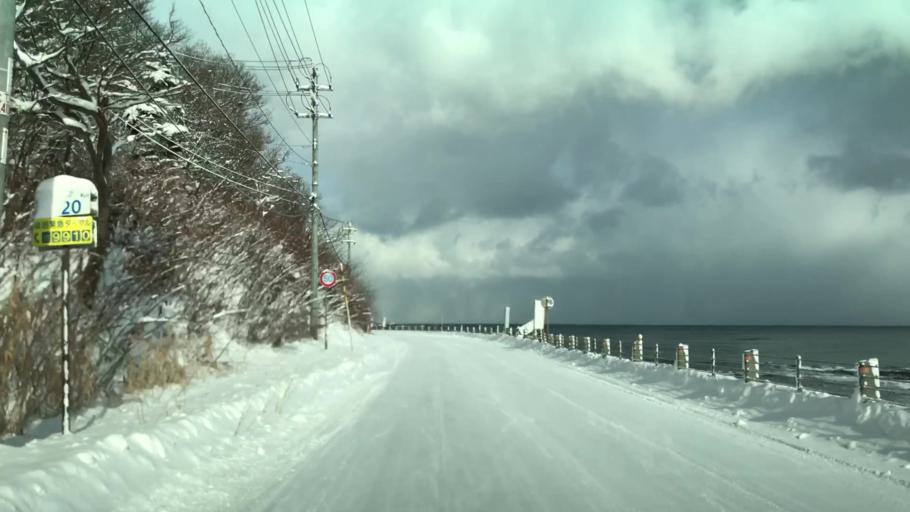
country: JP
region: Hokkaido
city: Yoichi
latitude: 43.2874
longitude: 140.6337
